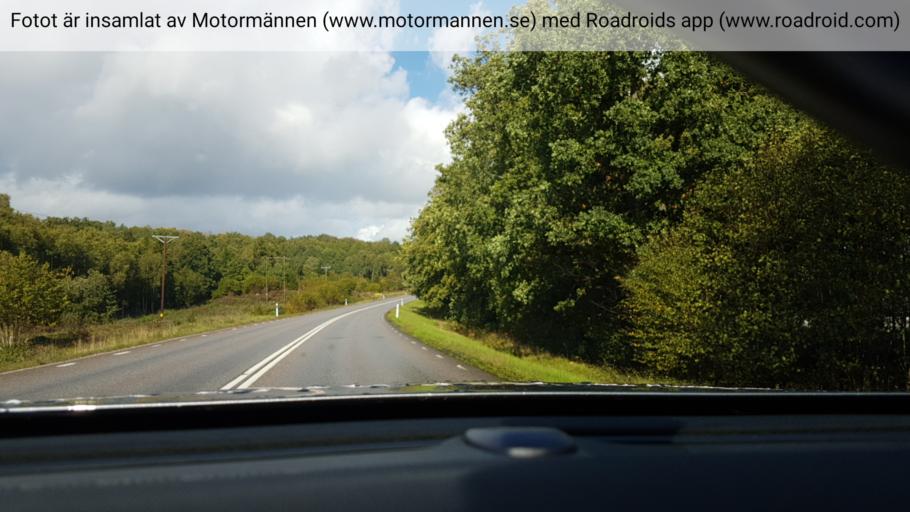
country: SE
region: Vaestra Goetaland
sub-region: Alingsas Kommun
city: Sollebrunn
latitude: 58.0571
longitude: 12.4655
